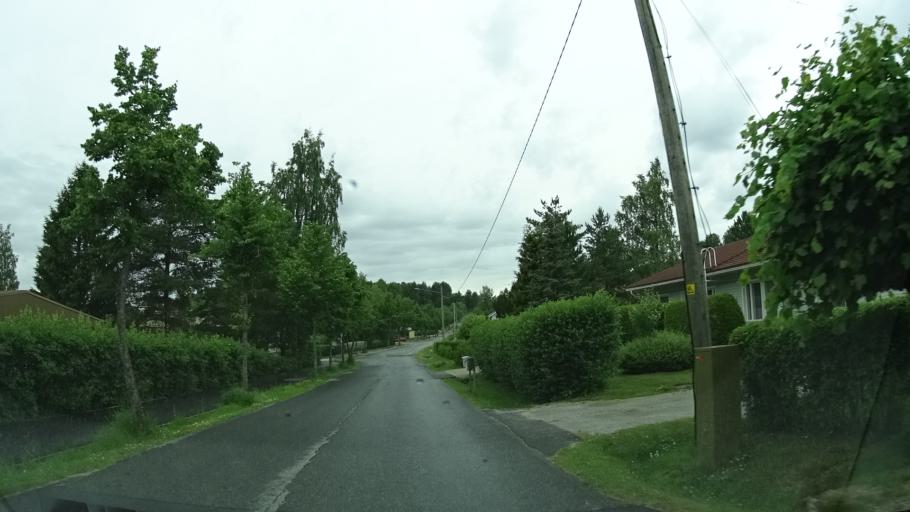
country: FI
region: Varsinais-Suomi
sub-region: Salo
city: Halikko
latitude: 60.4050
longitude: 23.0749
